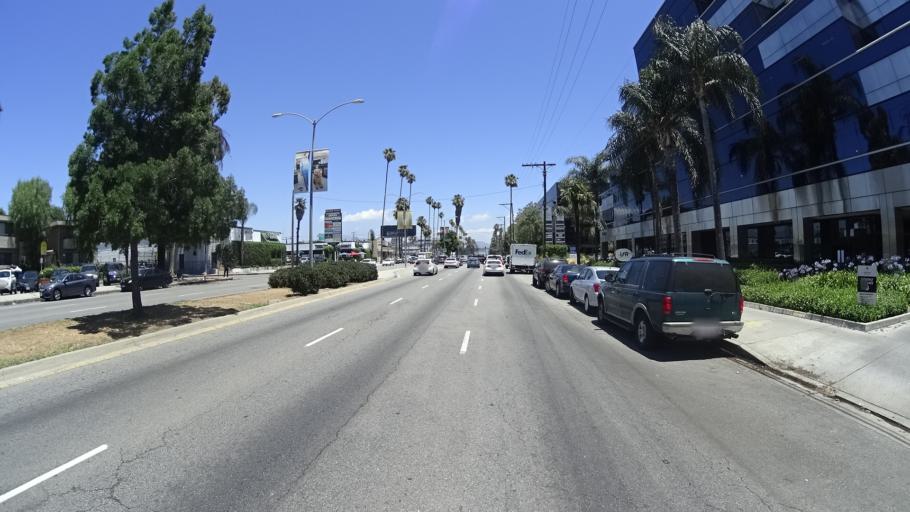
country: US
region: California
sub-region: Los Angeles County
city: Van Nuys
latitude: 34.2011
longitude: -118.4690
